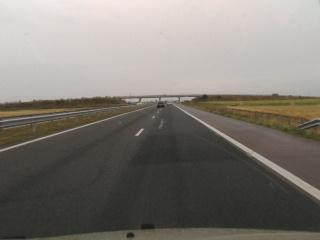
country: BG
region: Stara Zagora
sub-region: Obshtina Stara Zagora
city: Stara Zagora
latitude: 42.3666
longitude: 25.7857
